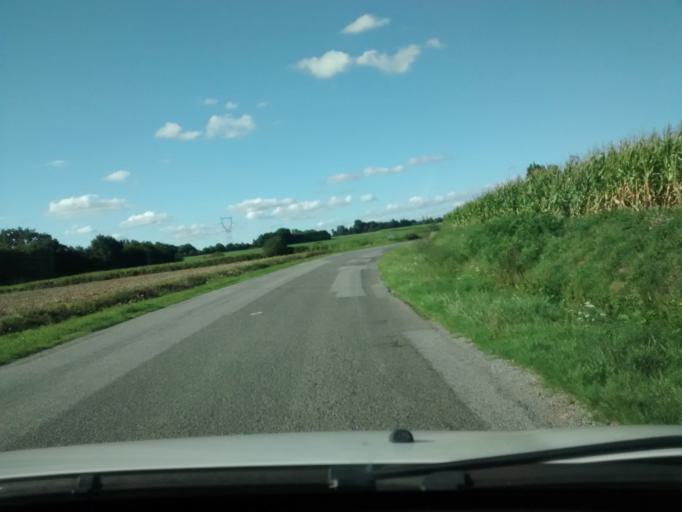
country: FR
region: Brittany
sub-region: Departement d'Ille-et-Vilaine
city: Nouvoitou
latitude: 48.0764
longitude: -1.5474
